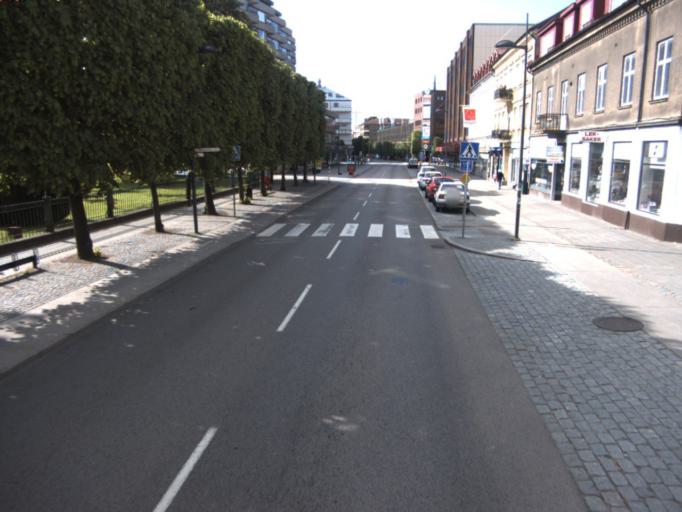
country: SE
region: Skane
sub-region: Helsingborg
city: Helsingborg
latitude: 56.0421
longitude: 12.7012
